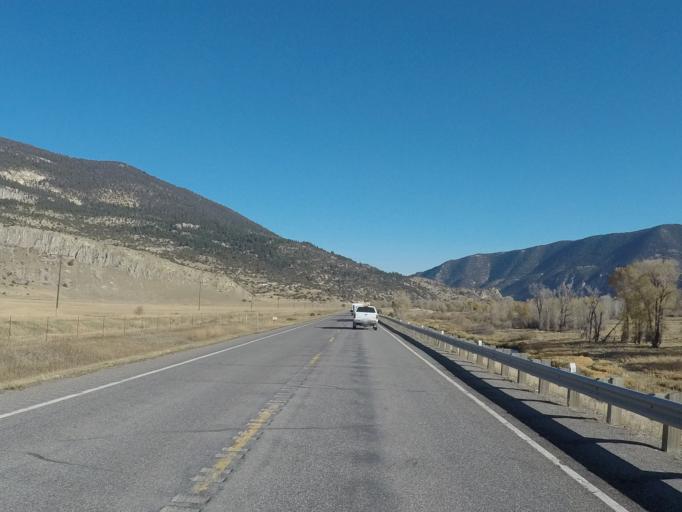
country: US
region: Montana
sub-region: Park County
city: Livingston
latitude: 45.5667
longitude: -110.5908
